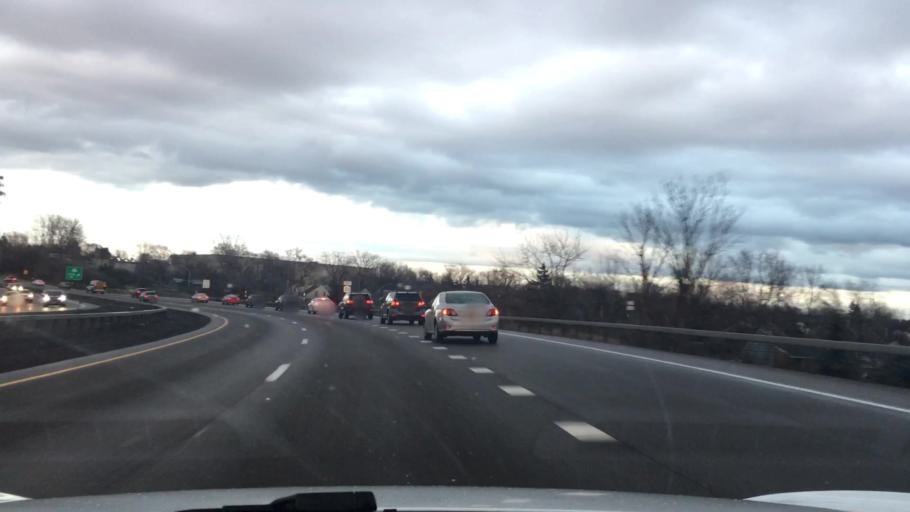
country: US
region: New York
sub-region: Erie County
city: Cheektowaga
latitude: 42.9306
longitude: -78.7613
